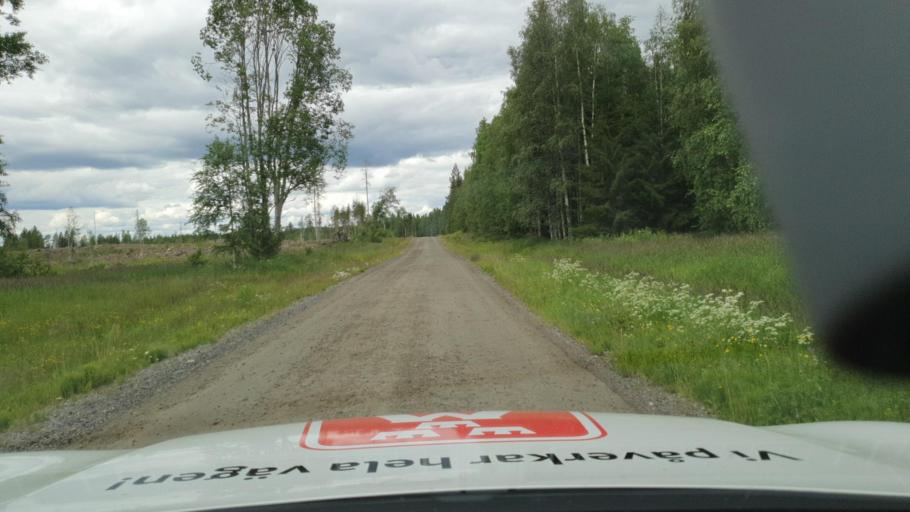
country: SE
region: Vaesterbotten
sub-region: Bjurholms Kommun
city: Bjurholm
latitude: 63.7852
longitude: 19.1139
